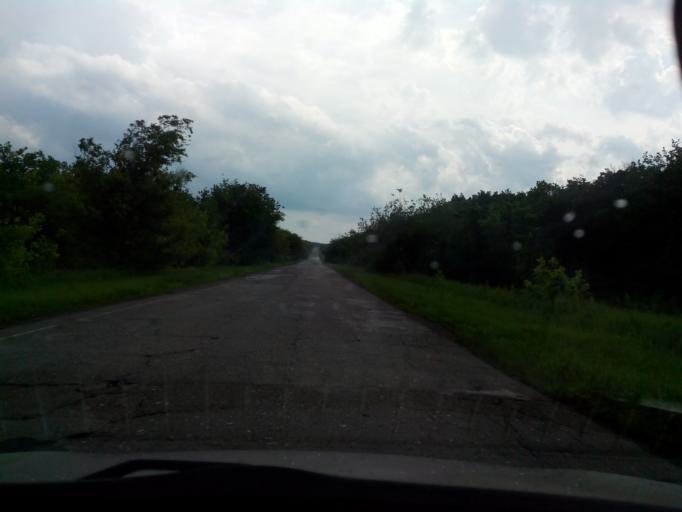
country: RU
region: Volgograd
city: Mikhaylovka
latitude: 49.9096
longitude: 42.9451
